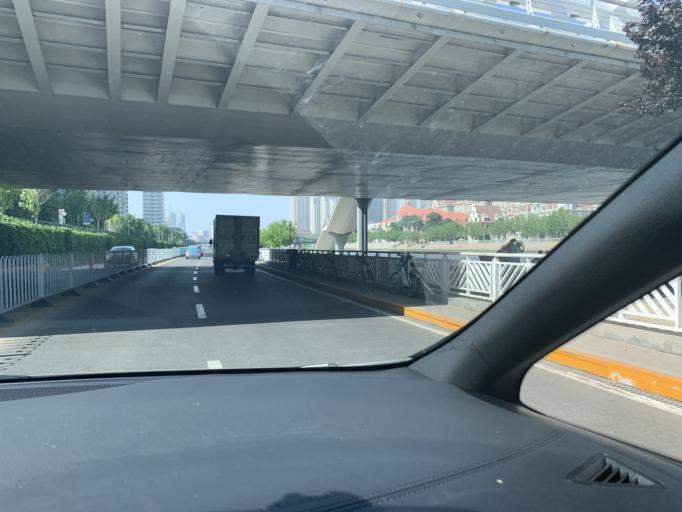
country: CN
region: Tianjin Shi
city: Gulou
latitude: 39.1357
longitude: 117.1870
